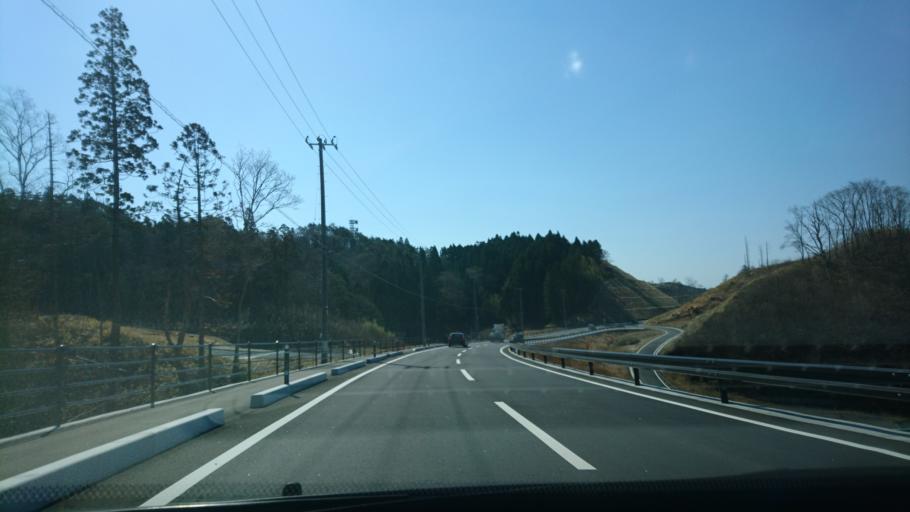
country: JP
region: Iwate
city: Ofunato
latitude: 38.8944
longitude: 141.5979
